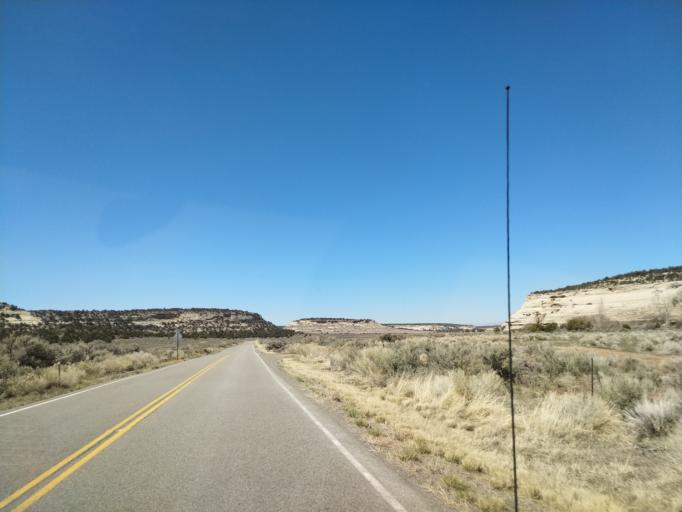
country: US
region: Colorado
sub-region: Mesa County
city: Redlands
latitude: 38.9827
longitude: -108.7962
